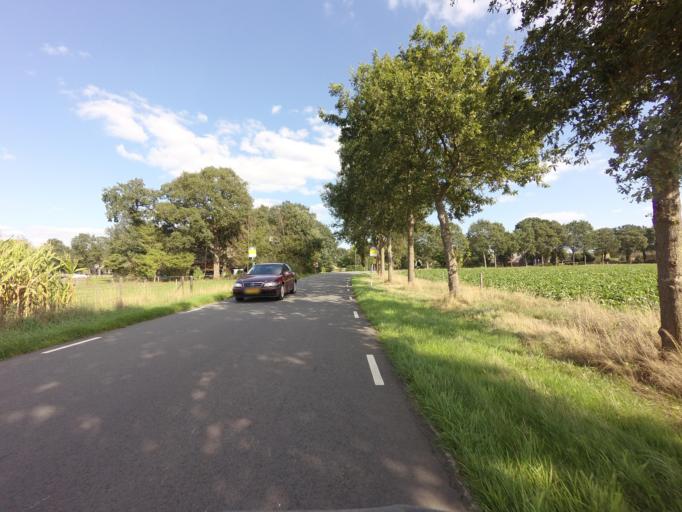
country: NL
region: Drenthe
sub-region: Gemeente Westerveld
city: Dwingeloo
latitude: 52.8330
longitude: 6.3907
